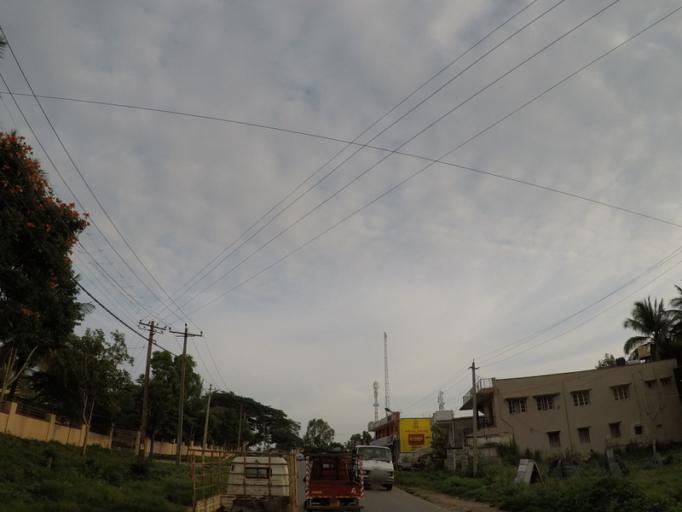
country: IN
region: Karnataka
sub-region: Hassan
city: Belur
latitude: 13.1739
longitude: 75.8748
